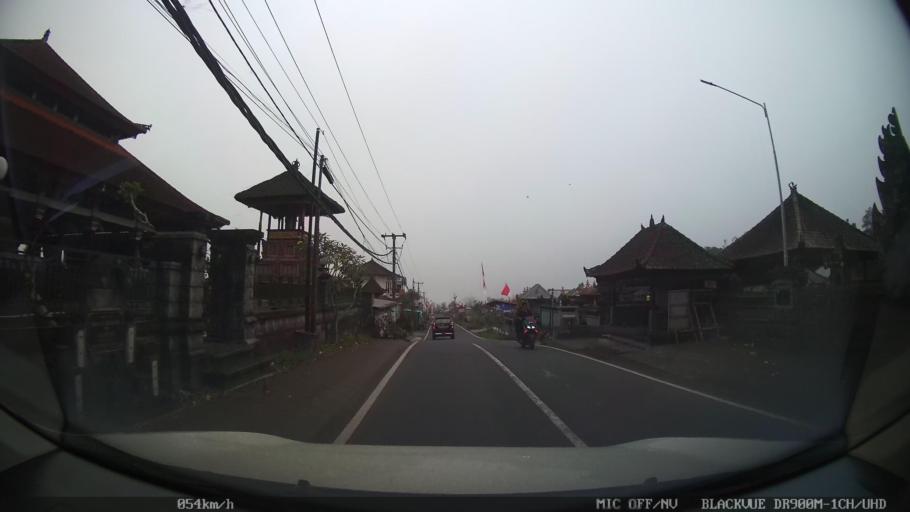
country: ID
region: Bali
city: Banjar Taro Kelod
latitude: -8.3086
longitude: 115.3051
